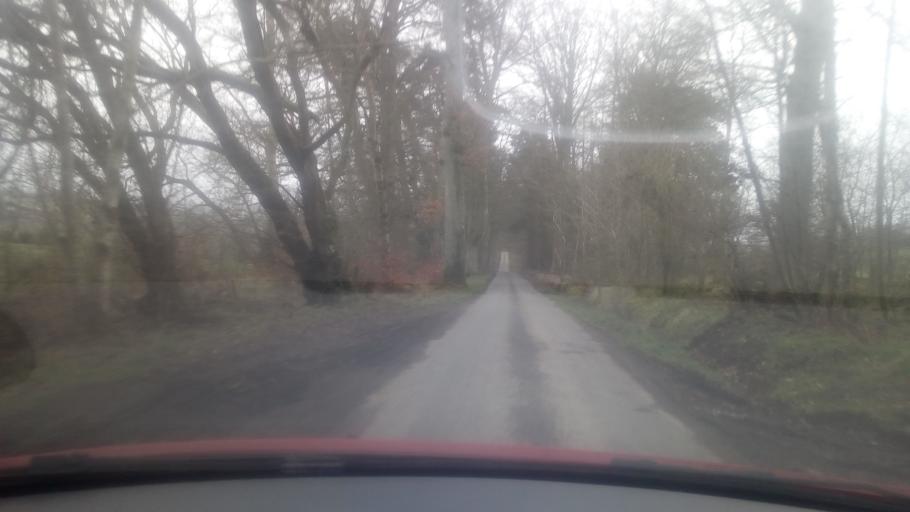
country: GB
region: Scotland
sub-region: The Scottish Borders
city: Jedburgh
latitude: 55.4338
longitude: -2.6403
